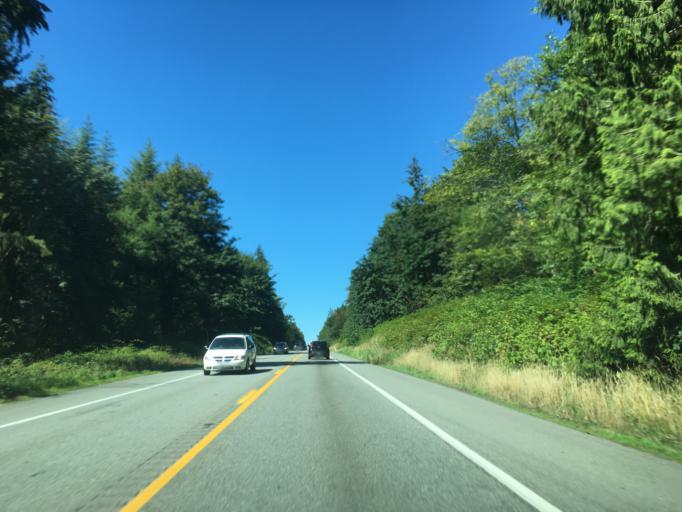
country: US
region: Washington
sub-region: Snohomish County
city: Sisco Heights
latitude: 48.0835
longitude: -122.1116
